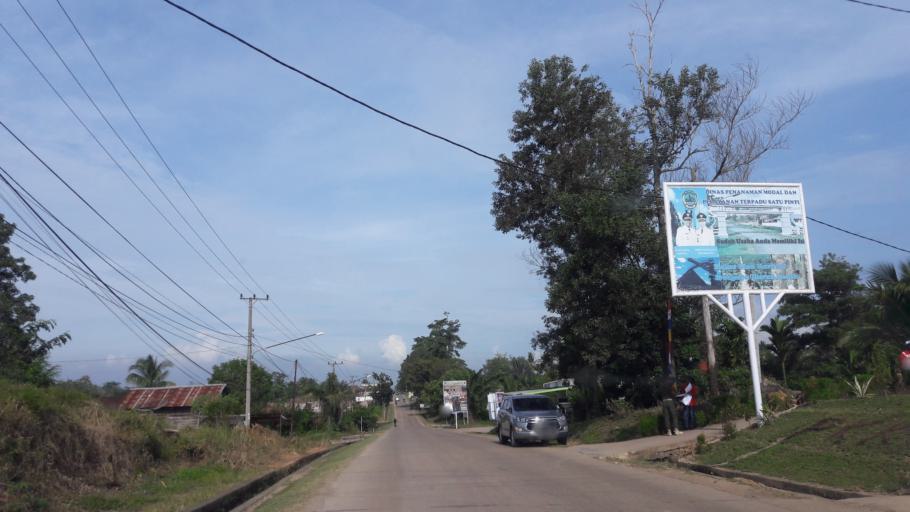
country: ID
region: South Sumatra
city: Gunungmegang Dalam
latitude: -3.2992
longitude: 103.8553
